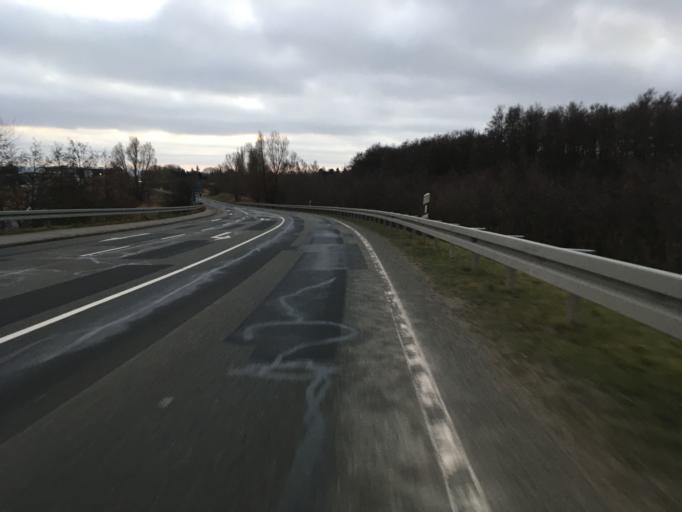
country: DE
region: Mecklenburg-Vorpommern
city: Sagard
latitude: 54.4869
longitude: 13.5769
